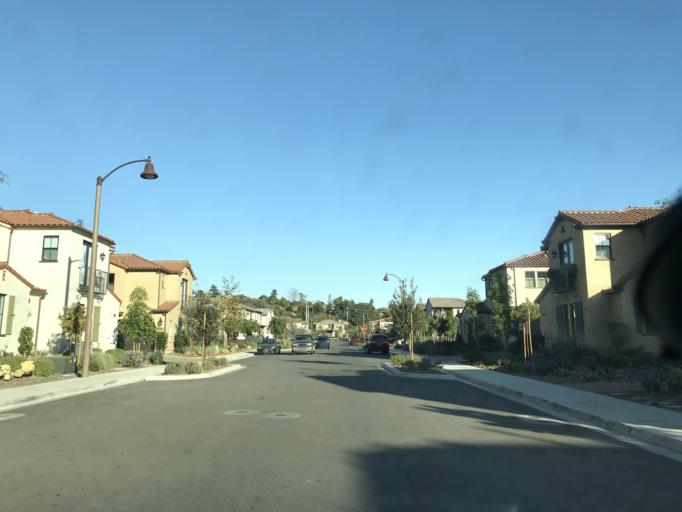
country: US
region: California
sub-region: Santa Barbara County
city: Goleta
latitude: 34.4490
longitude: -119.8118
